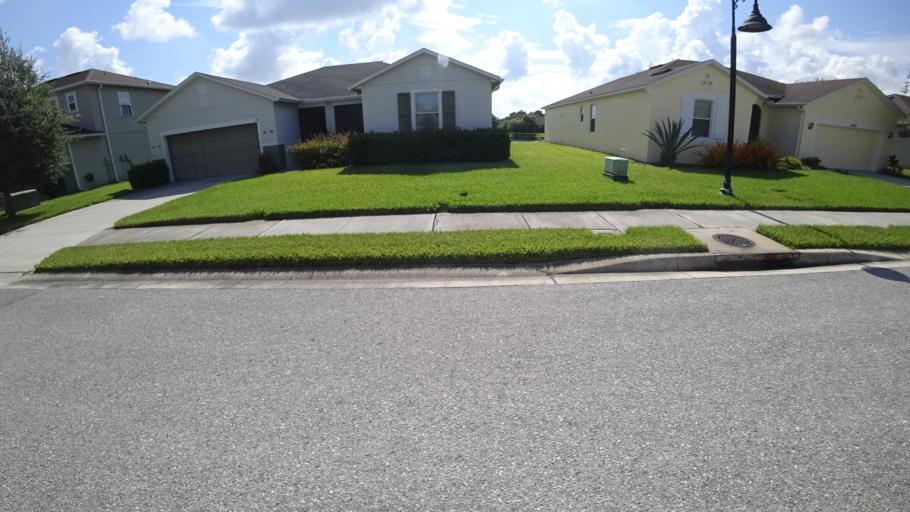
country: US
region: Florida
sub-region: Manatee County
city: Whitfield
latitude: 27.4276
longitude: -82.5617
